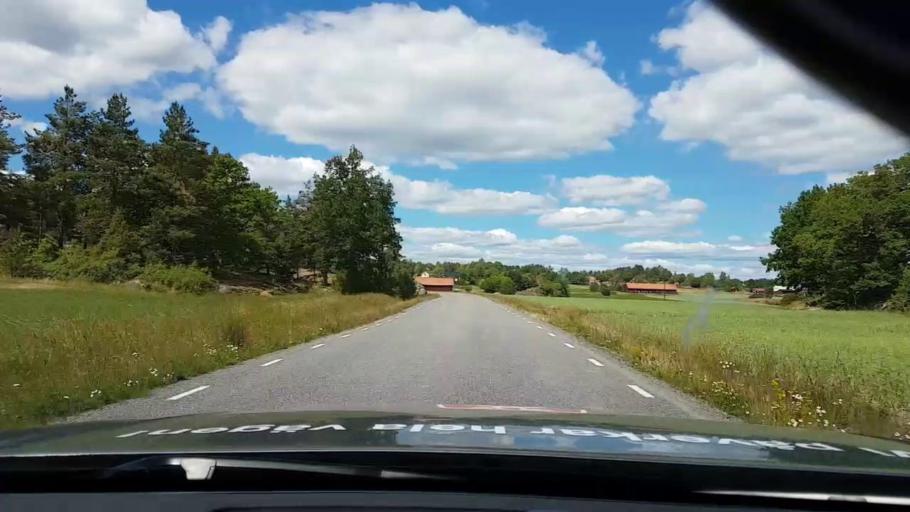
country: SE
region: Kalmar
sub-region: Vasterviks Kommun
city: Forserum
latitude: 58.0052
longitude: 16.5863
